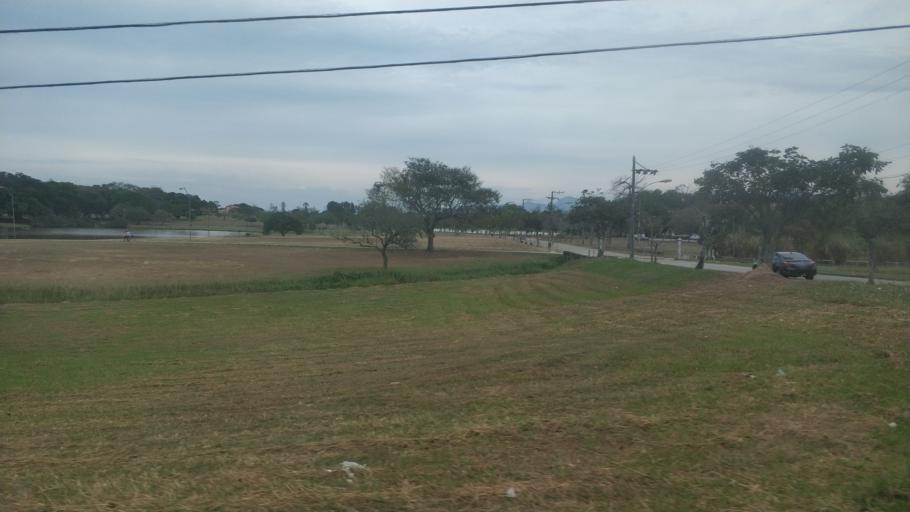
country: BR
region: Rio de Janeiro
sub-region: Seropedica
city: Seropedica
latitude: -22.7579
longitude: -43.6897
